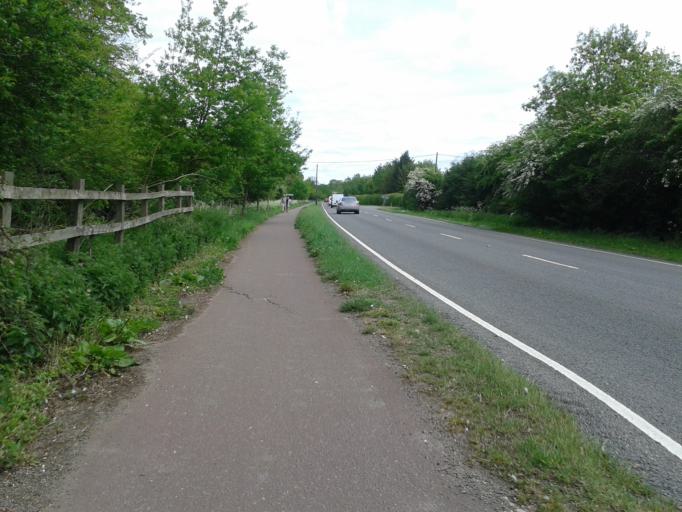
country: GB
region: England
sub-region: Cambridgeshire
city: Grantchester
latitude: 52.1972
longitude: 0.0878
